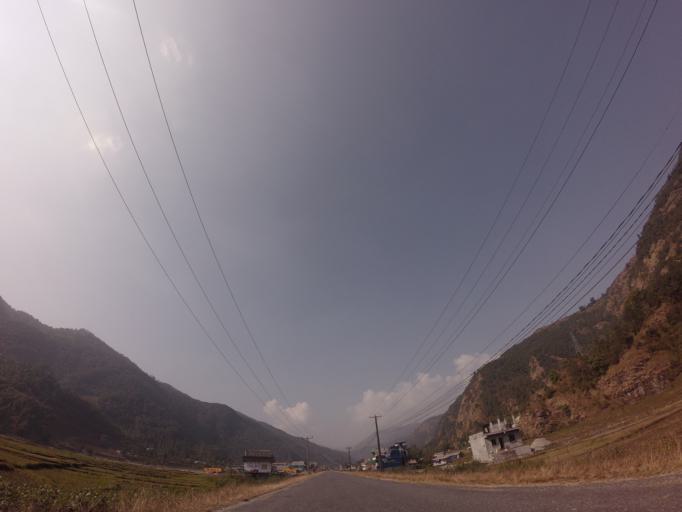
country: NP
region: Western Region
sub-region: Gandaki Zone
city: Pokhara
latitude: 28.2852
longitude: 83.9073
